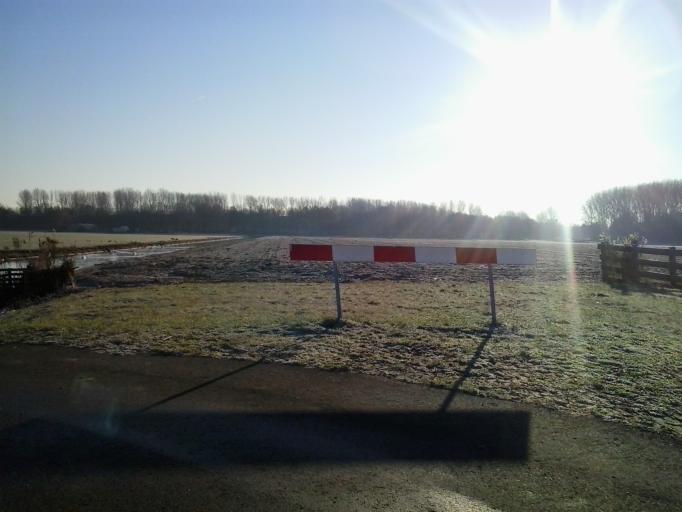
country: NL
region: South Holland
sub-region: Gemeente Lansingerland
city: Bergschenhoek
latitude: 51.9768
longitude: 4.5168
